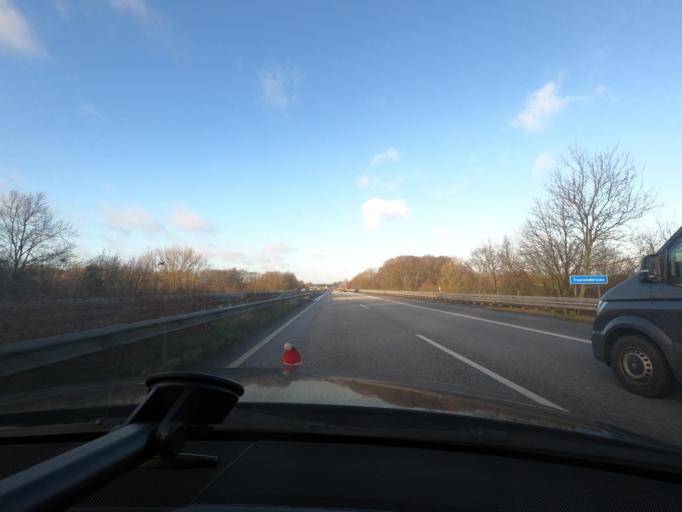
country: DE
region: Schleswig-Holstein
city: Tarp
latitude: 54.6723
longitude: 9.4255
